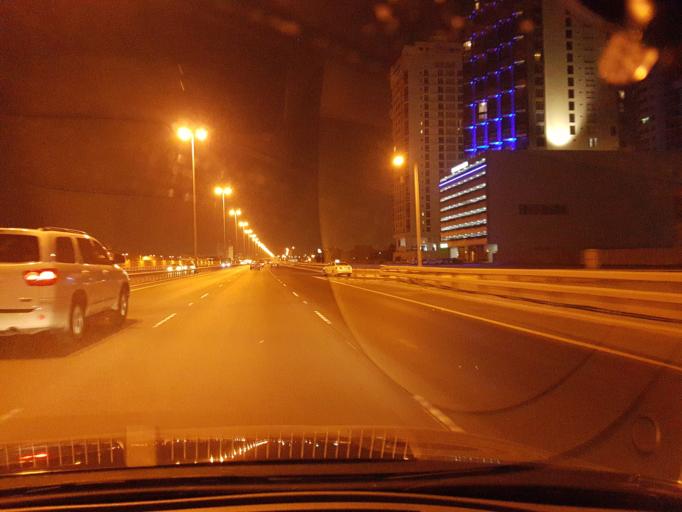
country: BH
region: Manama
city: Manama
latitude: 26.2134
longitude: 50.6209
